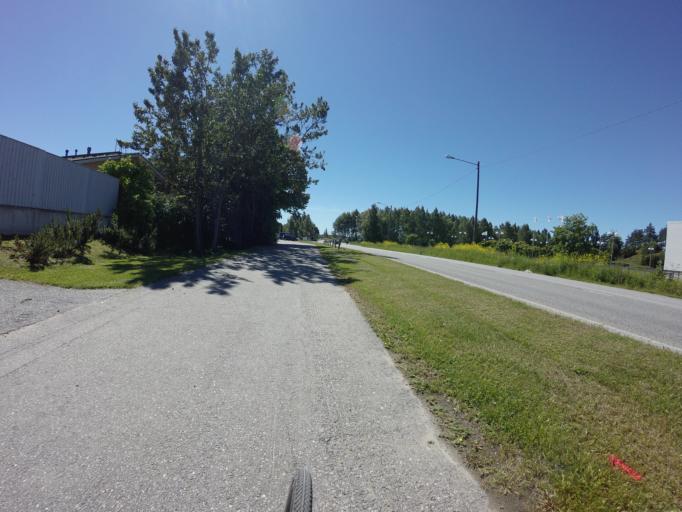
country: FI
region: Varsinais-Suomi
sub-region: Turku
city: Turku
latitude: 60.4784
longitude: 22.2964
